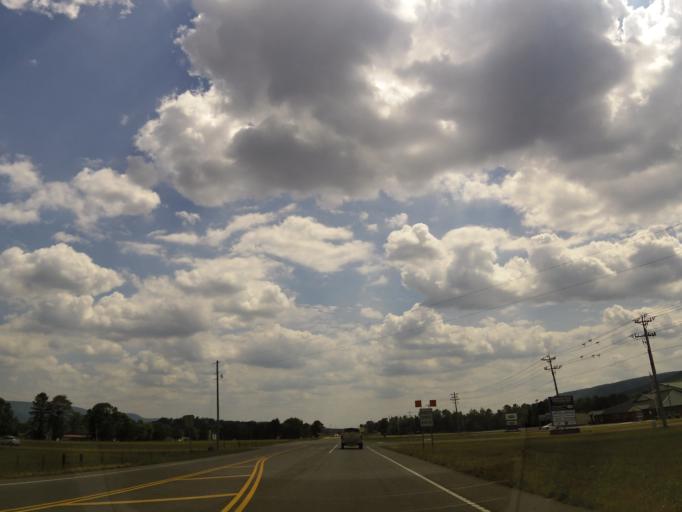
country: US
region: Tennessee
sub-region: Sequatchie County
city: Dunlap
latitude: 35.4021
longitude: -85.3706
